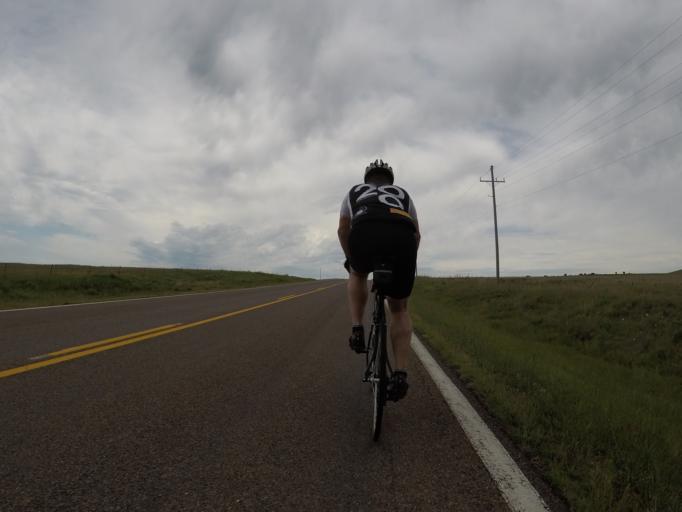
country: US
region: Kansas
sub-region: Wabaunsee County
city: Alma
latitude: 38.8699
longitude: -96.1734
